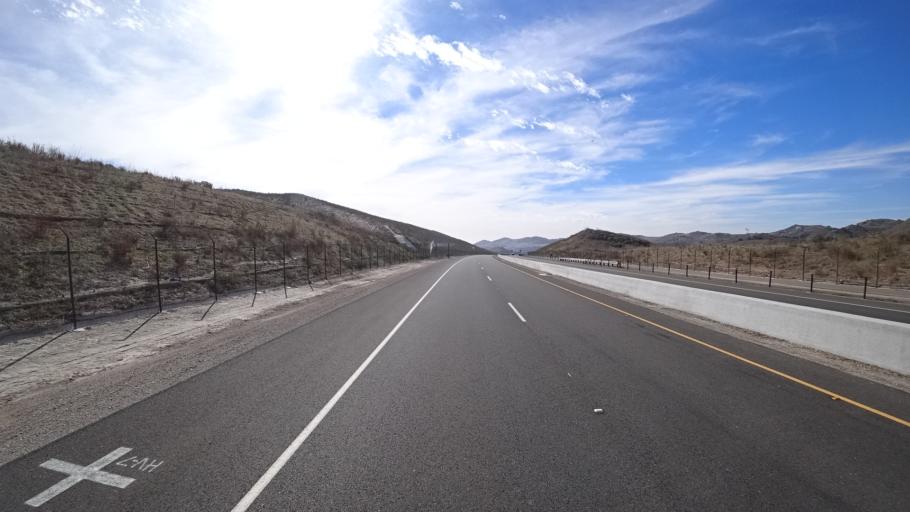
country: US
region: California
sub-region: Orange County
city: Las Flores
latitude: 33.5809
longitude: -117.6096
